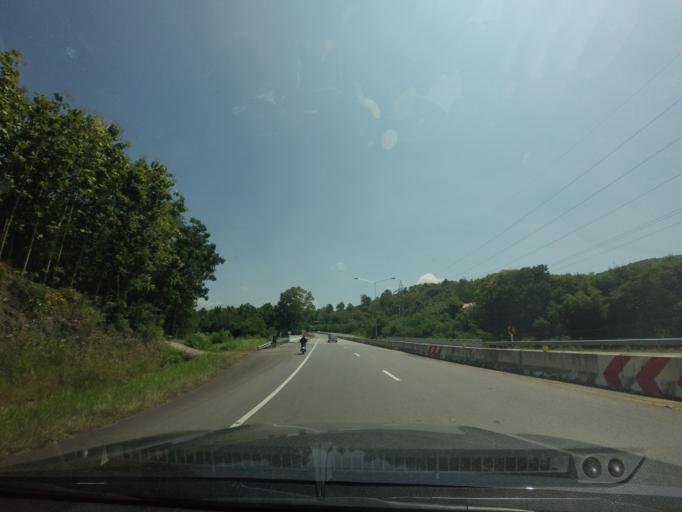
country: TH
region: Phetchabun
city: Lom Sak
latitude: 16.7635
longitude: 101.1413
